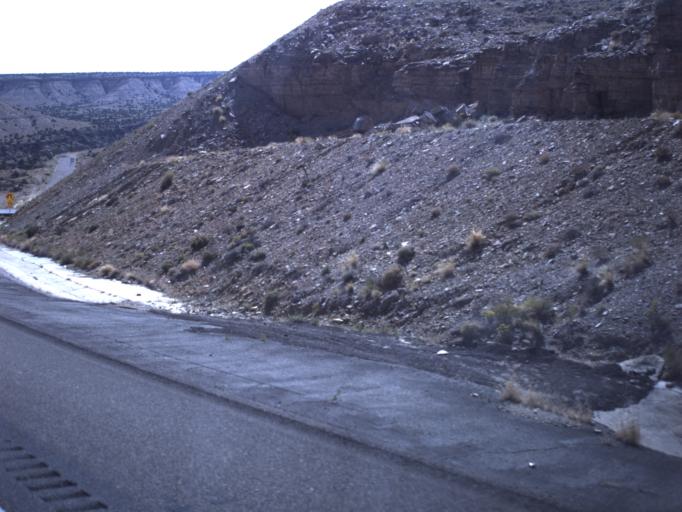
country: US
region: Utah
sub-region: Carbon County
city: East Carbon City
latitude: 38.9347
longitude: -110.4636
